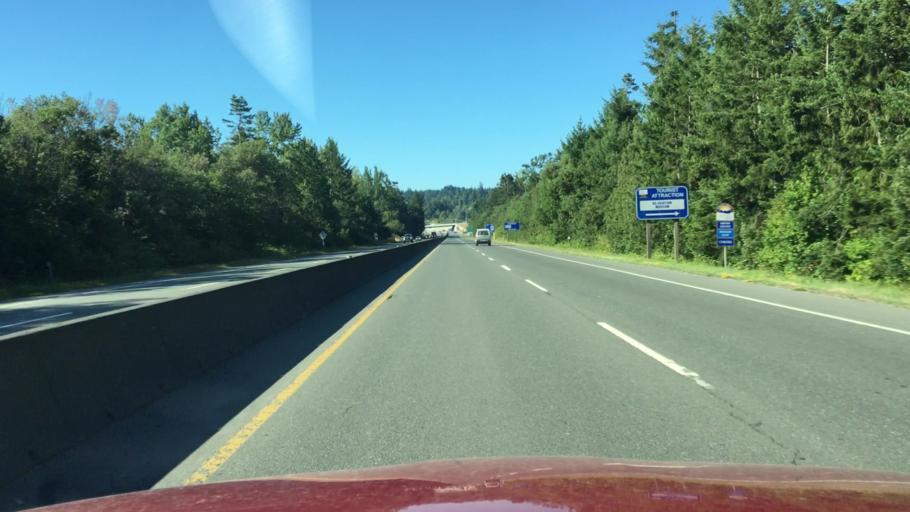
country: CA
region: British Columbia
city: North Saanich
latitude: 48.6390
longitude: -123.4081
